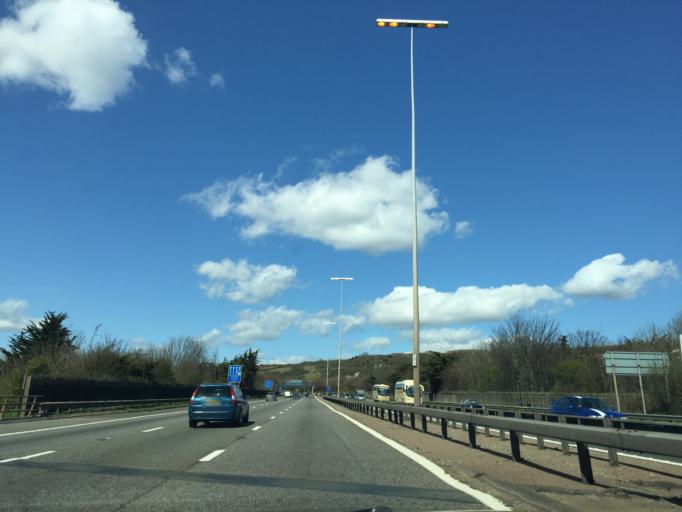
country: GB
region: England
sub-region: Portsmouth
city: Cosham
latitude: 50.8487
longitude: -1.1019
